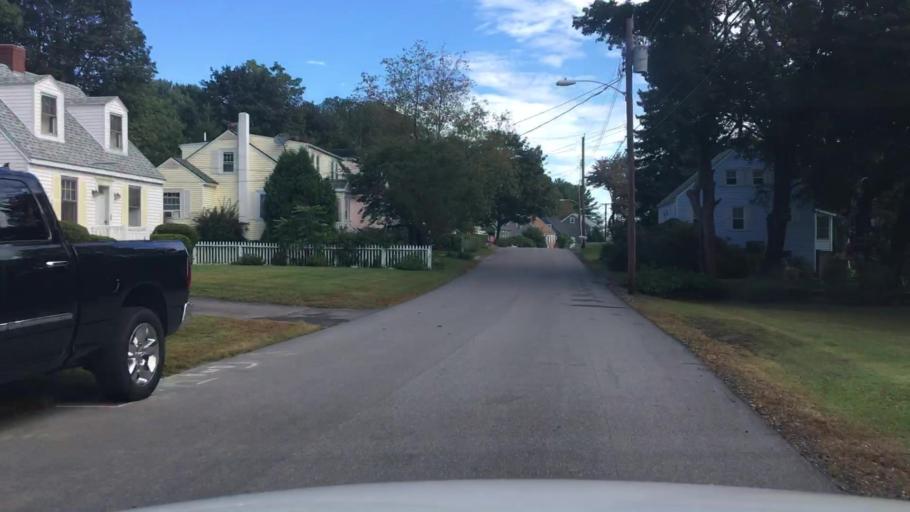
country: US
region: Maine
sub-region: York County
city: Kittery
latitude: 43.0868
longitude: -70.7289
